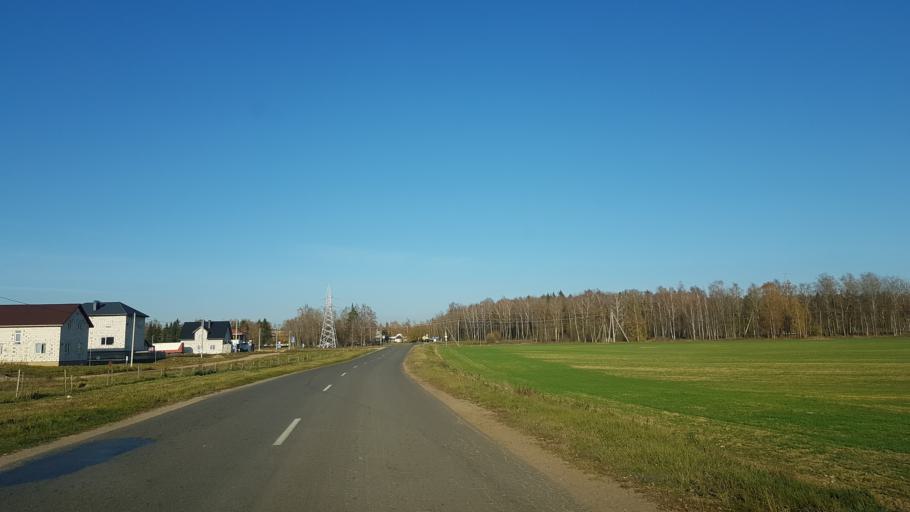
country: BY
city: Fanipol
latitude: 53.7271
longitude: 27.3296
